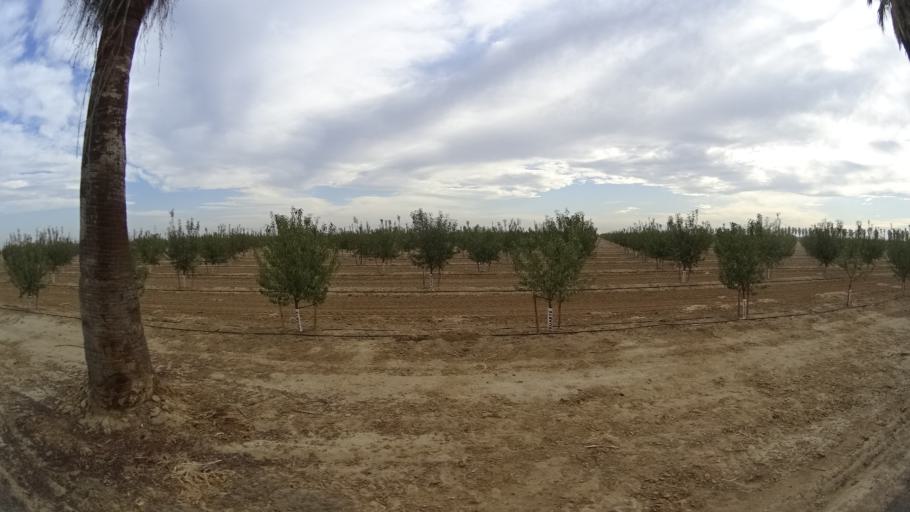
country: US
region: California
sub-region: Kern County
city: Rosedale
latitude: 35.4375
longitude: -119.1721
